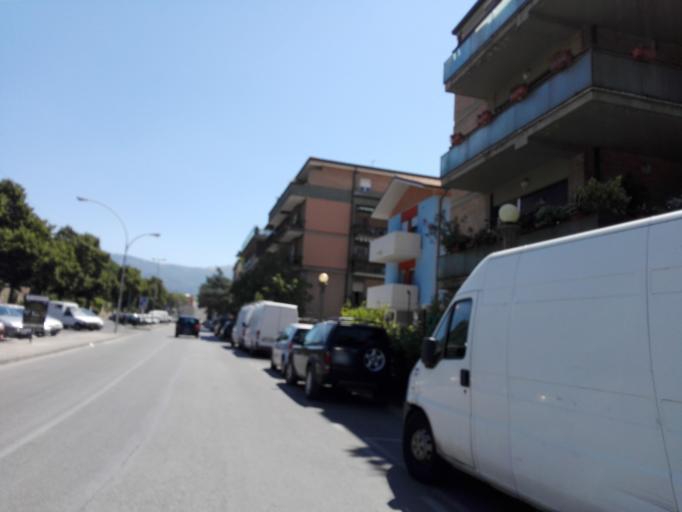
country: IT
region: Umbria
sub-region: Provincia di Perugia
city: Foligno
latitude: 42.9521
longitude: 12.6990
